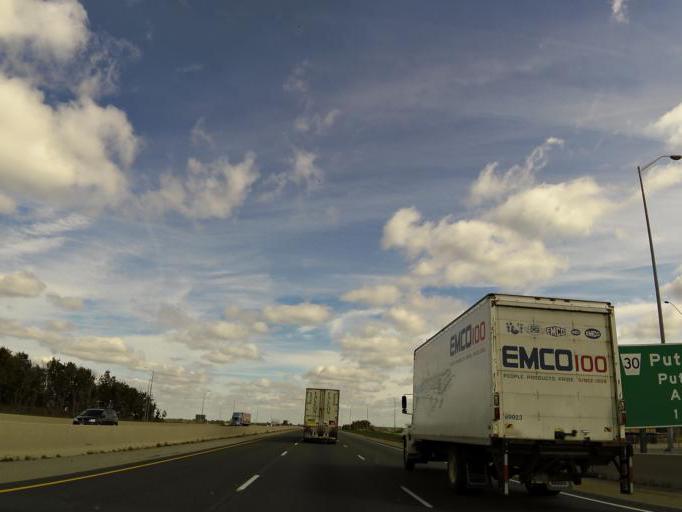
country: CA
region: Ontario
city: Dorchester
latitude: 42.9732
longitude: -80.9679
